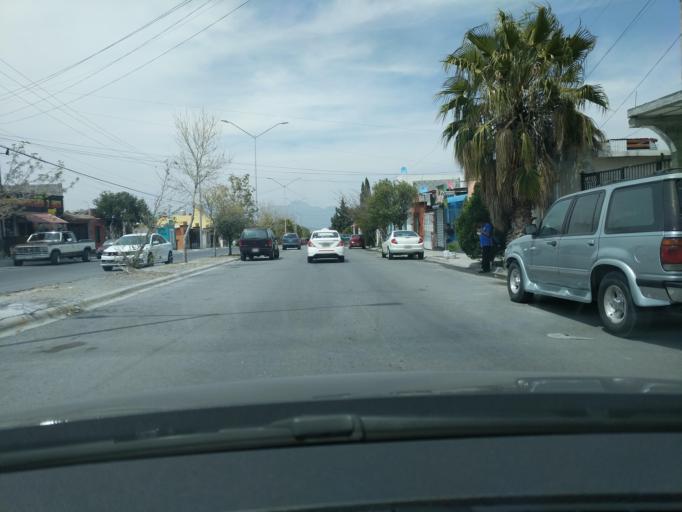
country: MX
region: Coahuila
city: Saltillo
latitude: 25.3494
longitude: -101.0100
